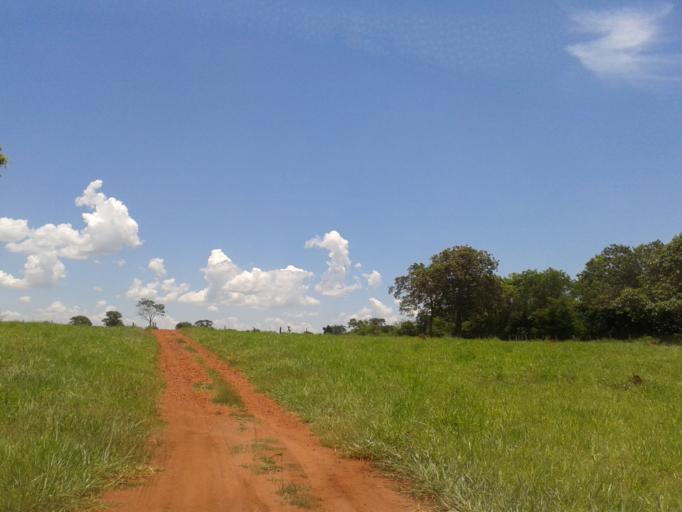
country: BR
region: Minas Gerais
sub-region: Santa Vitoria
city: Santa Vitoria
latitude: -19.1268
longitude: -50.5621
